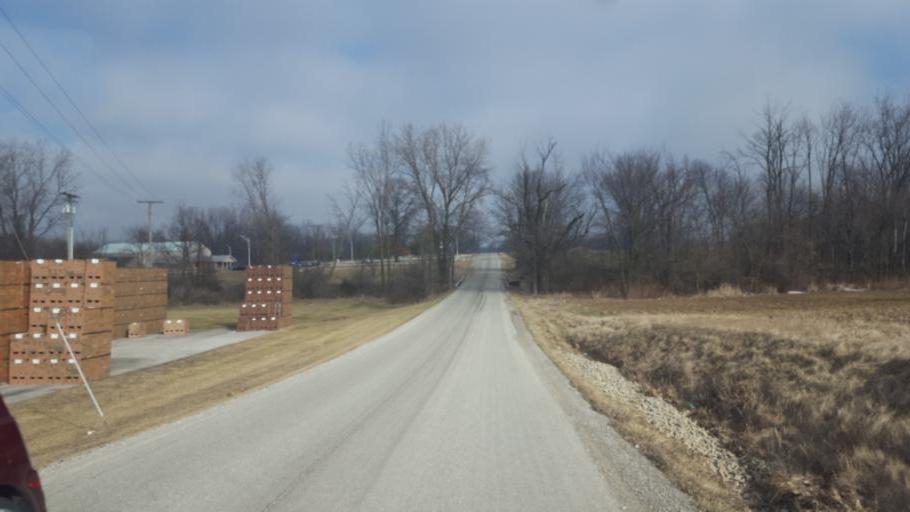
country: US
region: Ohio
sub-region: Crawford County
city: Galion
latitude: 40.6578
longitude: -82.8594
